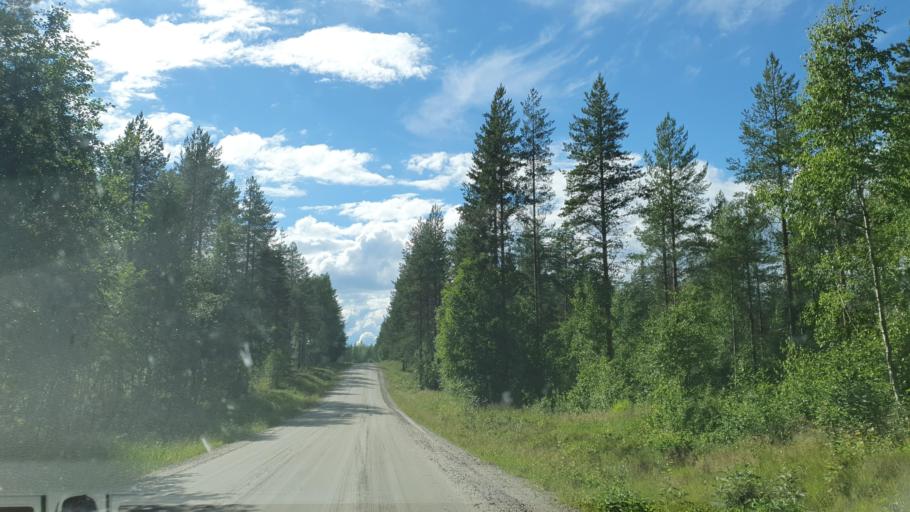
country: FI
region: Kainuu
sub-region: Kehys-Kainuu
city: Kuhmo
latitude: 64.1399
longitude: 29.6936
